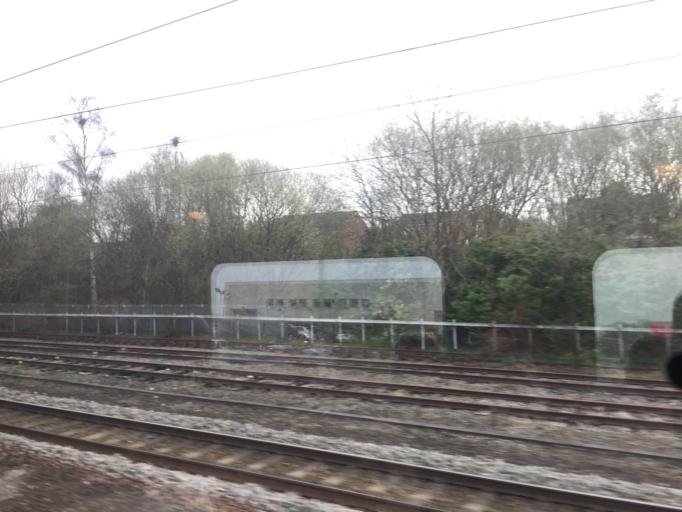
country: GB
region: England
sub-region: Warrington
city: Warrington
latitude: 53.3905
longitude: -2.6039
